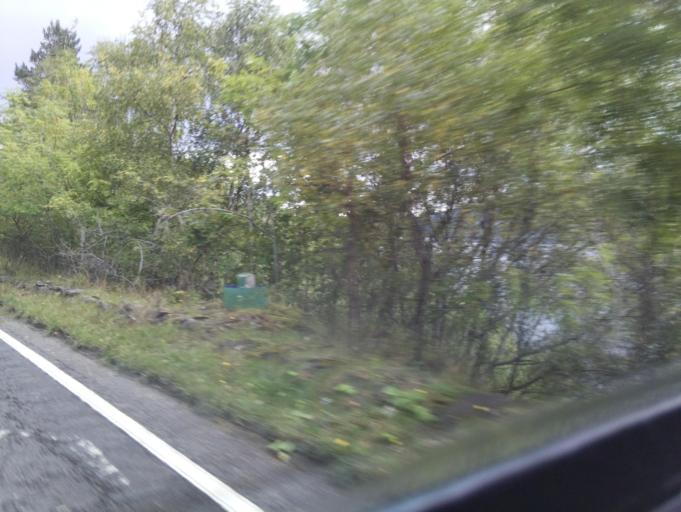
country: GB
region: Scotland
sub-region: Highland
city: Beauly
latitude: 57.3174
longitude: -4.4515
